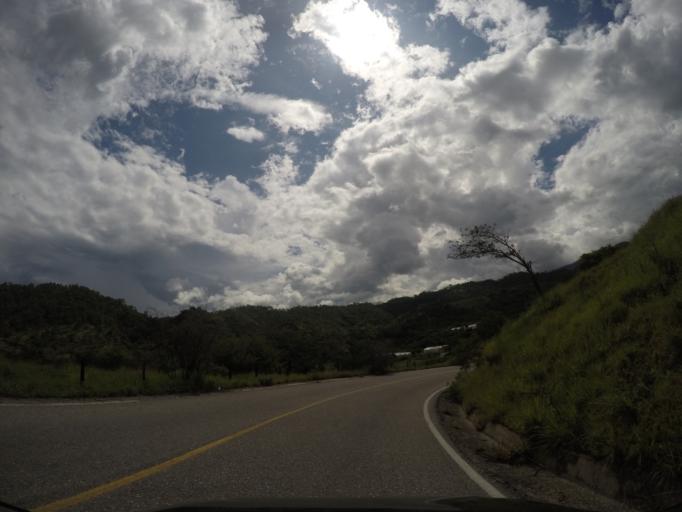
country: MX
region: Oaxaca
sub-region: San Jeronimo Coatlan
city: San Cristobal Honduras
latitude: 16.4245
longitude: -97.0713
